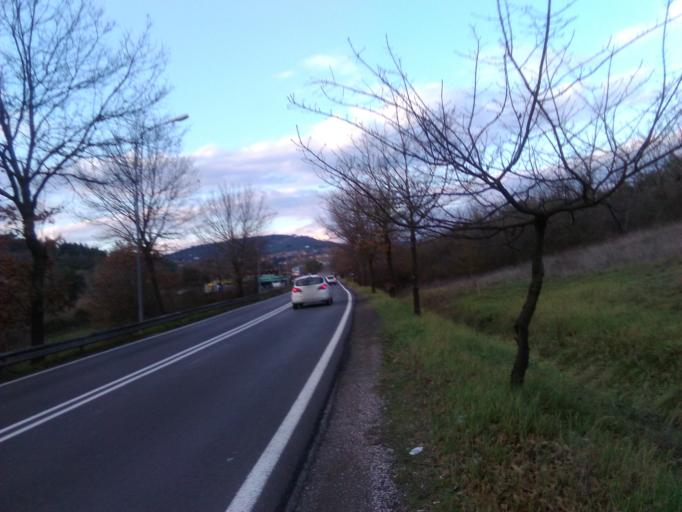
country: IT
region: Umbria
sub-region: Provincia di Perugia
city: Lacugnano
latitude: 43.0907
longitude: 12.3588
